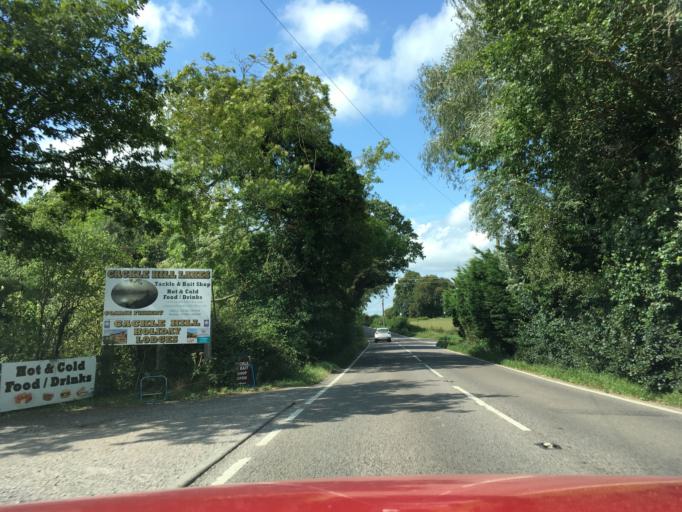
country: GB
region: England
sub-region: Kent
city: Headcorn
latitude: 51.1312
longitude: 0.6452
